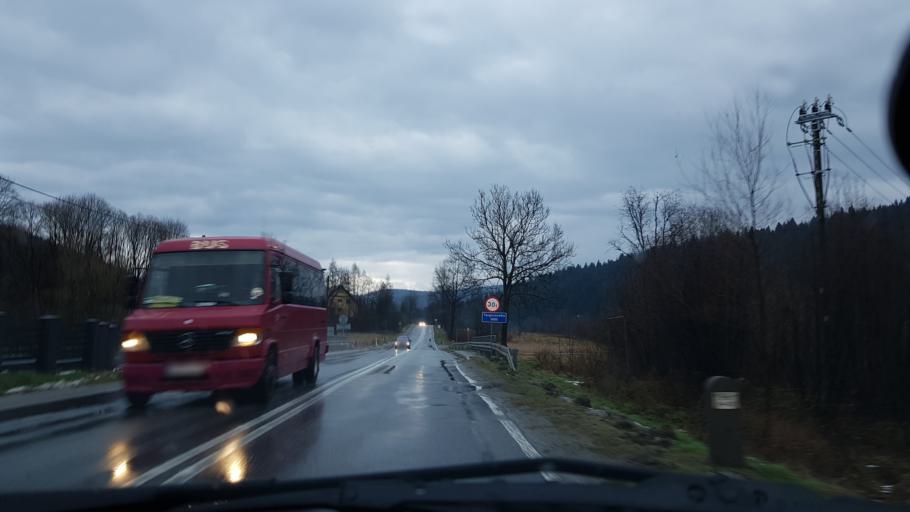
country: PL
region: Lesser Poland Voivodeship
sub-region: Powiat suski
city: Kukow
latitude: 49.7403
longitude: 19.4619
